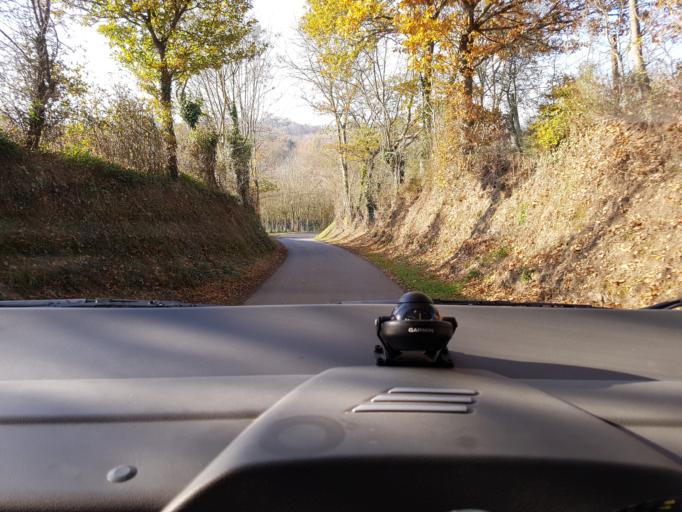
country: FR
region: Lower Normandy
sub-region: Departement du Calvados
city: Saint-Remy
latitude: 48.9373
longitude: -0.5419
